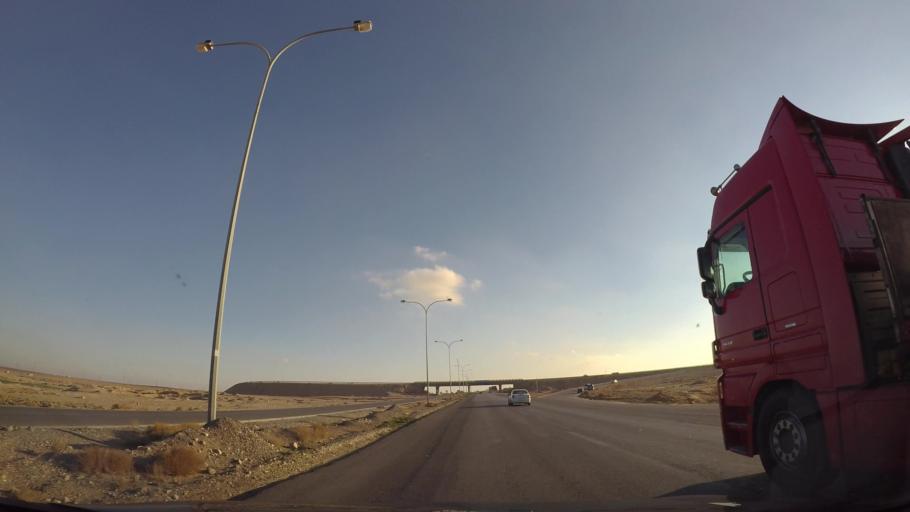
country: JO
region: Tafielah
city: Busayra
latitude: 30.5789
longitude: 35.7998
